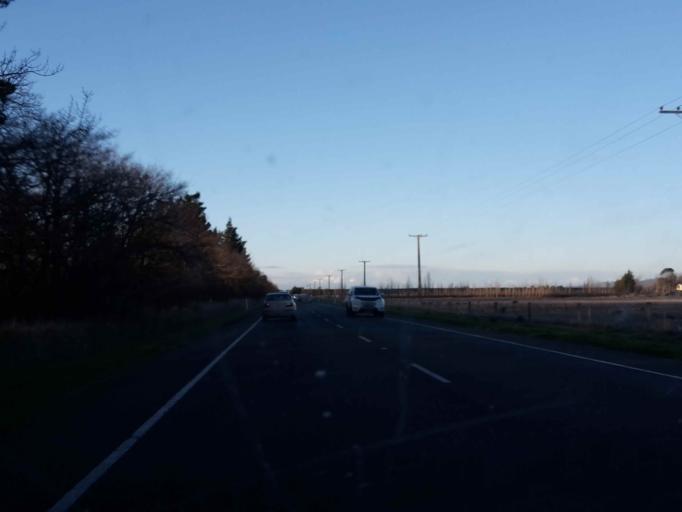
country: NZ
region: Canterbury
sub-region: Selwyn District
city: Burnham
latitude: -43.6260
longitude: 172.2860
